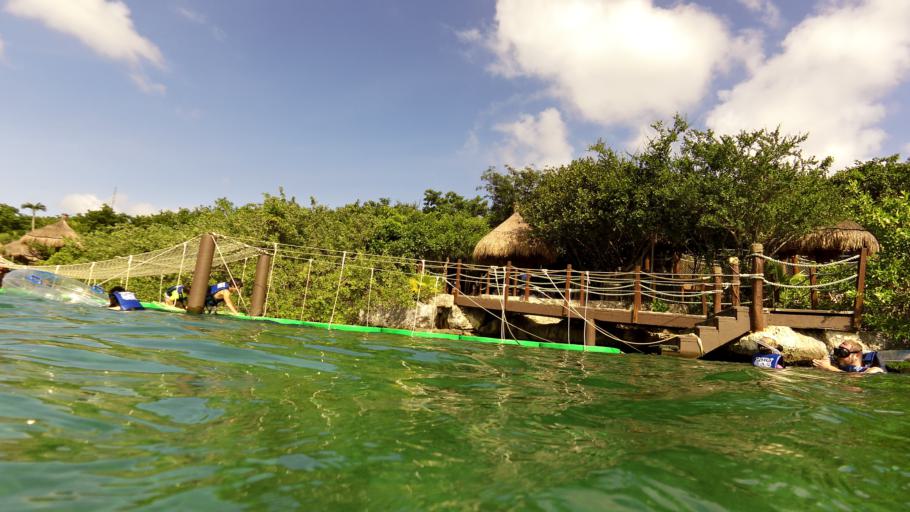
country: MX
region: Quintana Roo
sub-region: Tulum
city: Ciudad Chemuyil
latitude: 20.3183
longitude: -87.3581
